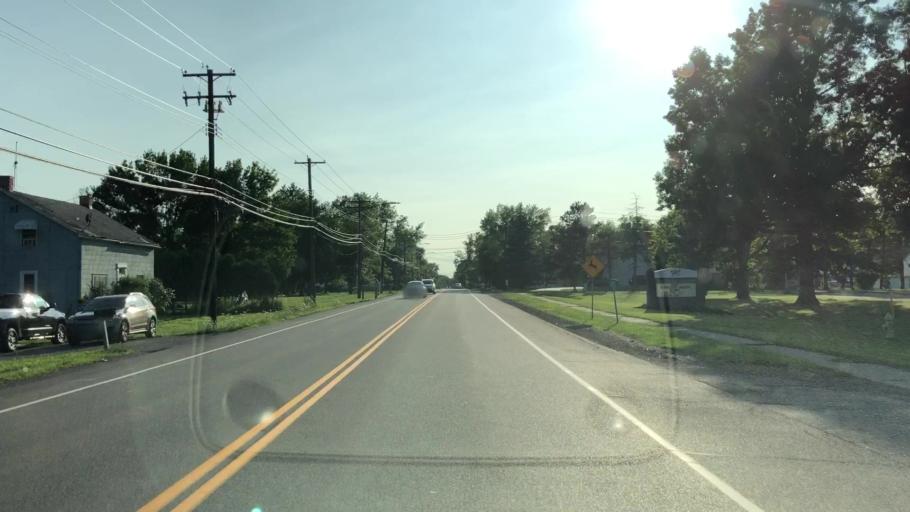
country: US
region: New York
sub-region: Erie County
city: Cheektowaga
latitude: 42.8571
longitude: -78.7316
